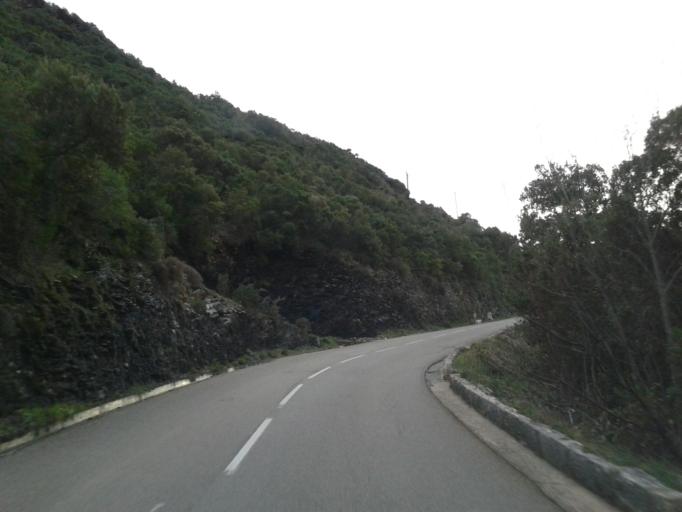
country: FR
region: Corsica
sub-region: Departement de la Haute-Corse
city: Saint-Florent
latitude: 42.7603
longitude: 9.3443
